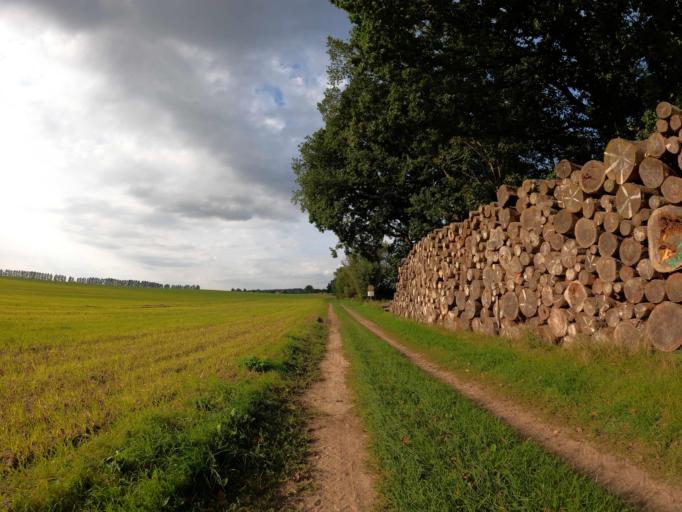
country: DE
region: Mecklenburg-Vorpommern
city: Klink
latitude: 53.4472
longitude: 12.5245
